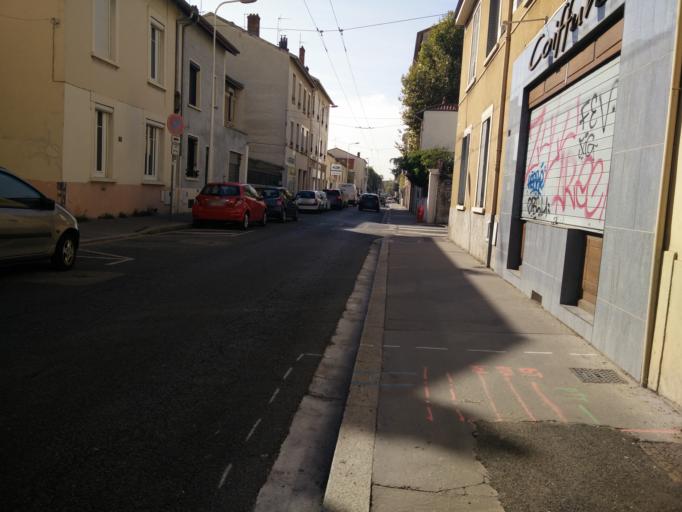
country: FR
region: Rhone-Alpes
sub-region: Departement du Rhone
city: Villeurbanne
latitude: 45.7470
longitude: 4.8803
